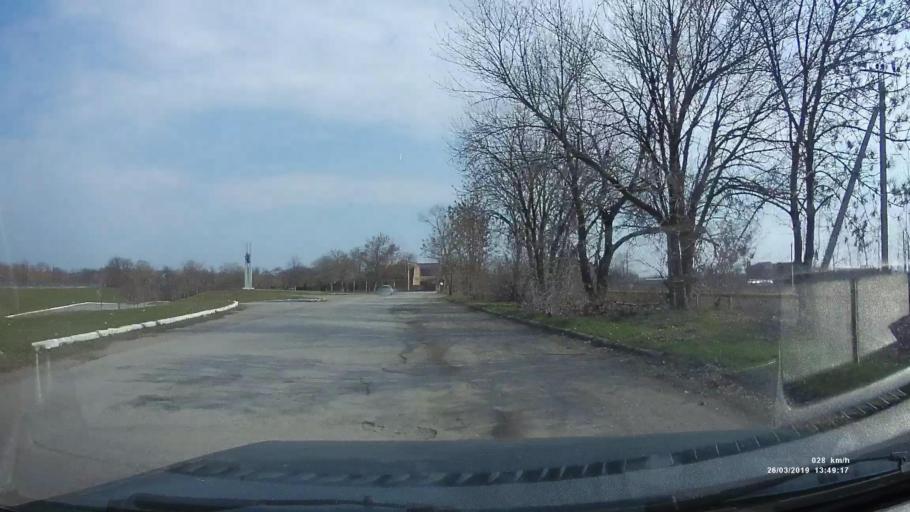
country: RU
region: Rostov
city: Novobessergenovka
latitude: 47.1910
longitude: 38.8647
